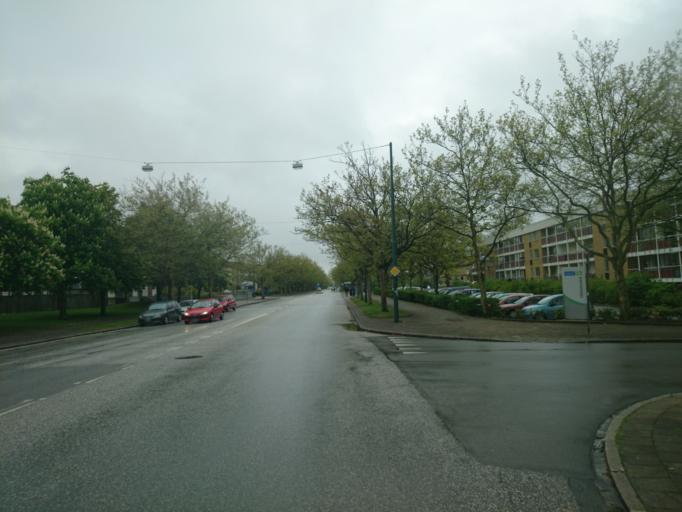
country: SE
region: Skane
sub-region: Malmo
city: Malmoe
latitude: 55.5884
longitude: 13.0362
